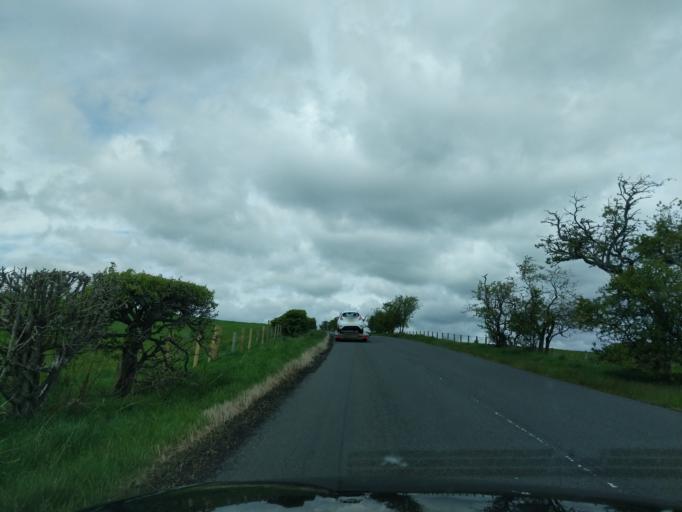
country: GB
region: Scotland
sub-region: The Scottish Borders
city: Earlston
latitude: 55.7013
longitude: -2.6025
